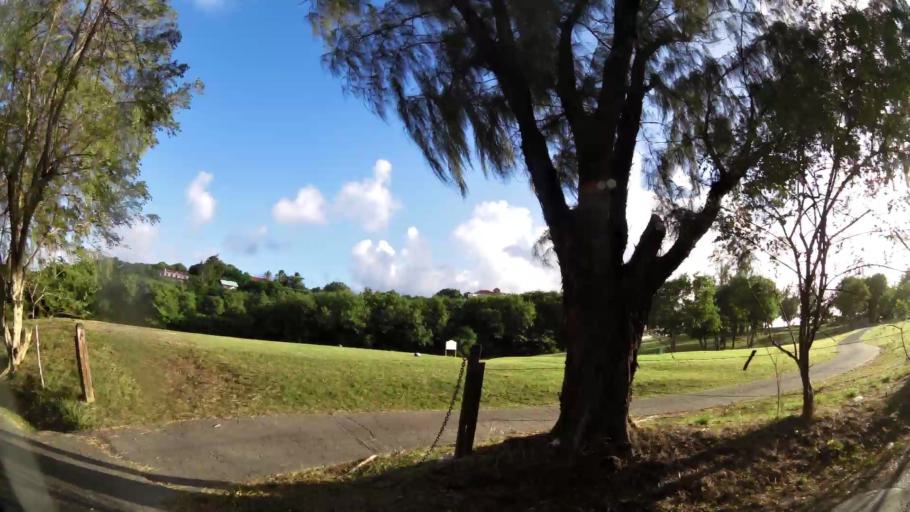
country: LC
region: Gros-Islet
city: Gros Islet
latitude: 14.0969
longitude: -60.9424
